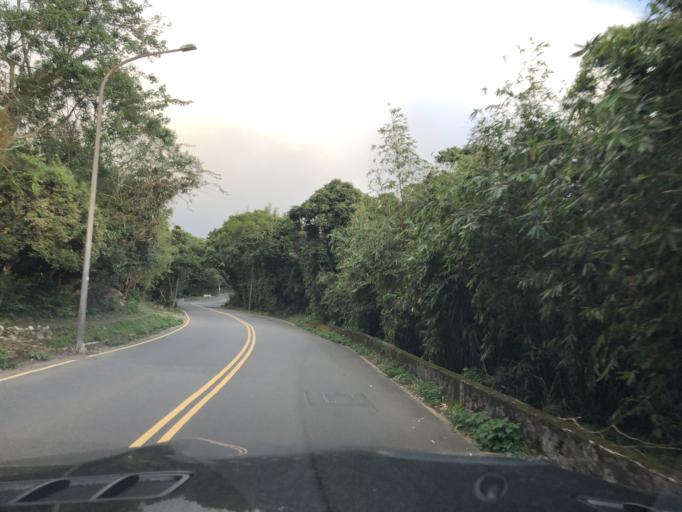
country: TW
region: Taipei
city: Taipei
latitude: 25.1517
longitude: 121.5598
